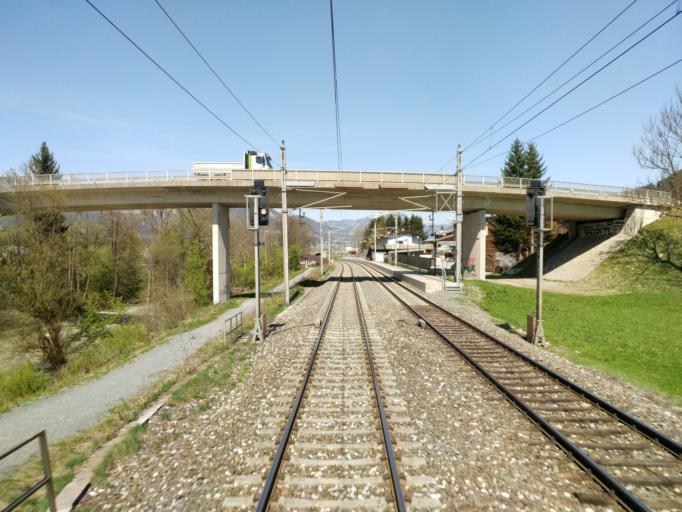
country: AT
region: Tyrol
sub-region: Politischer Bezirk Kitzbuhel
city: Oberndorf in Tirol
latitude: 47.4957
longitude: 12.3894
